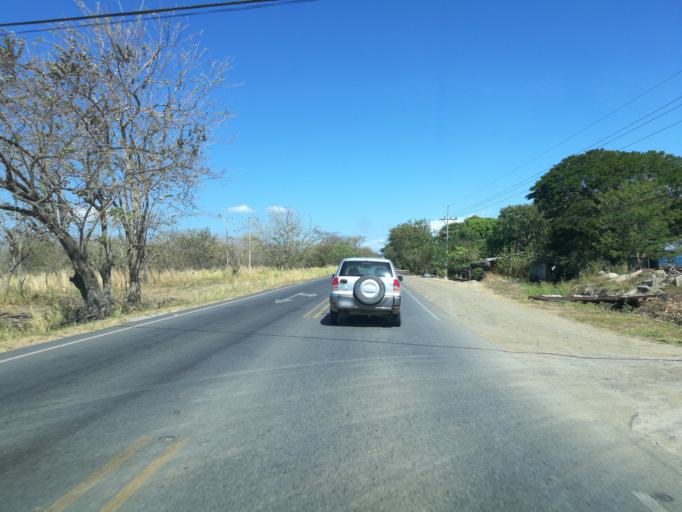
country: CR
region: Guanacaste
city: Liberia
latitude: 10.6527
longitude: -85.4653
